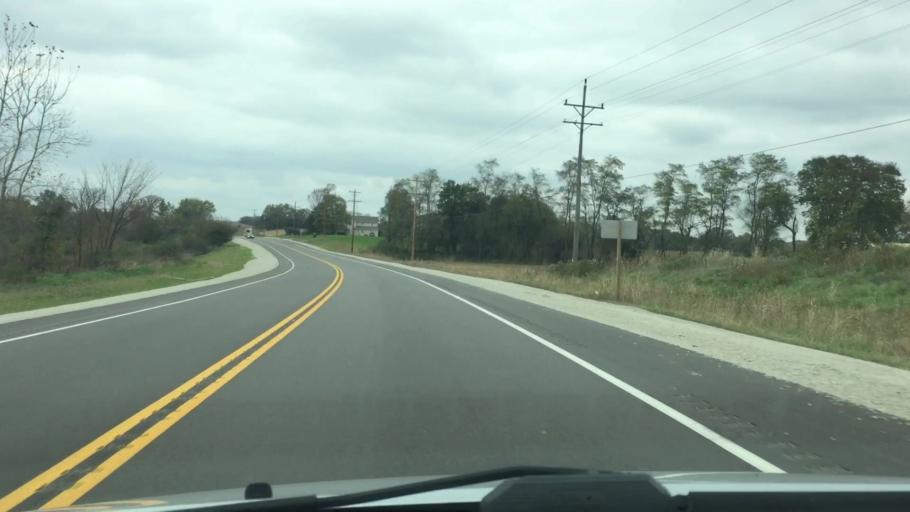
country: US
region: Wisconsin
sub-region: Walworth County
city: Whitewater
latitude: 42.8487
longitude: -88.7830
